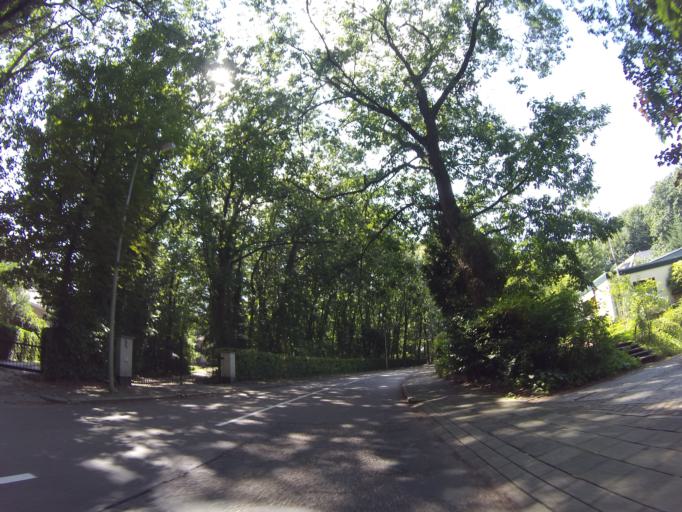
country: NL
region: Utrecht
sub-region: Gemeente Zeist
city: Zeist
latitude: 52.1270
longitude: 5.2499
